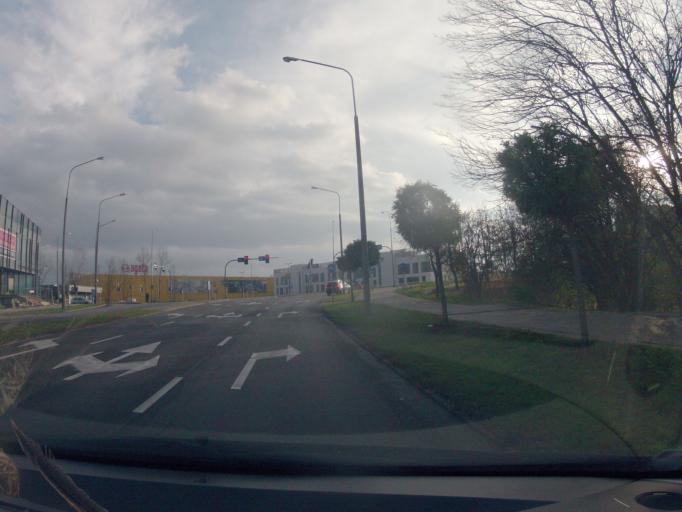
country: PL
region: Opole Voivodeship
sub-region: Powiat opolski
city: Opole
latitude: 50.6696
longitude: 17.9509
